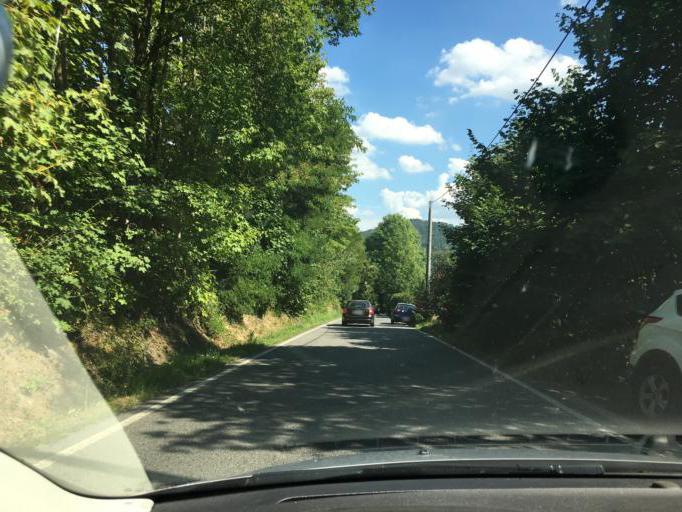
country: CZ
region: Liberecky
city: Mala Skala
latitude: 50.6448
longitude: 15.1755
